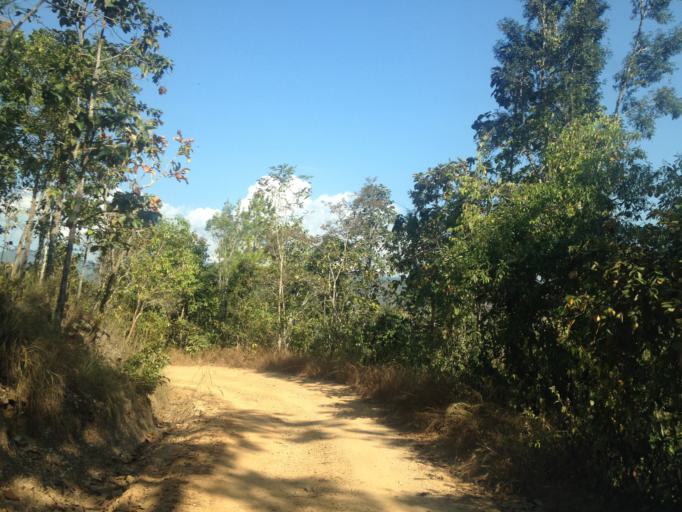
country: TH
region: Mae Hong Son
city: Ban Huai I Huak
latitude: 18.1245
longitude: 98.2011
